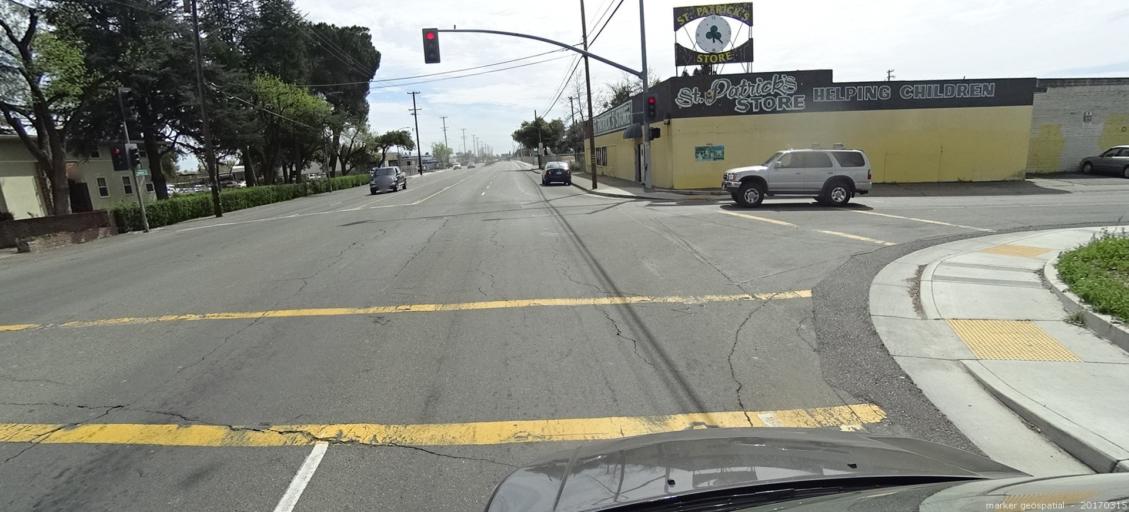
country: US
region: California
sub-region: Sacramento County
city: Parkway
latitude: 38.5184
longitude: -121.4701
